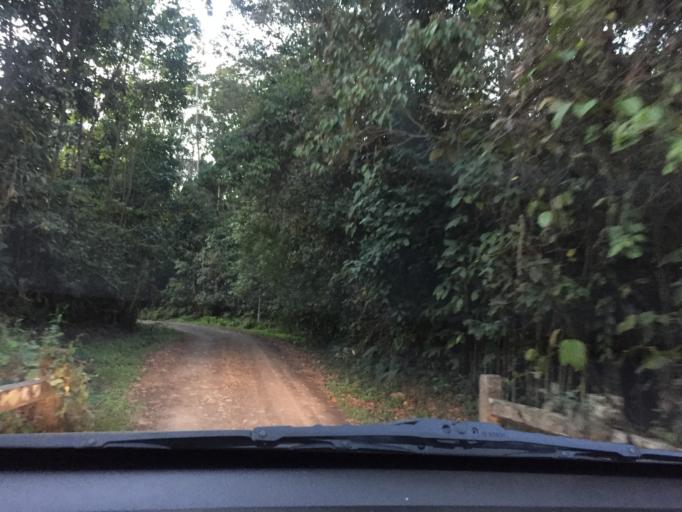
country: CO
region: Cundinamarca
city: Zipacon
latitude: 4.7102
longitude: -74.4080
